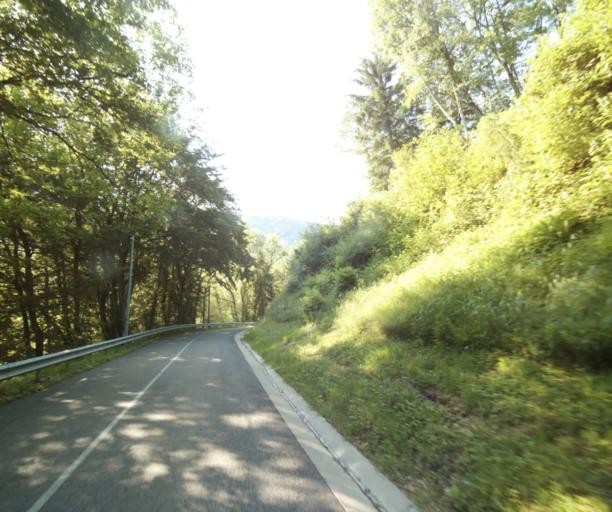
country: FR
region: Rhone-Alpes
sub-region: Departement de la Haute-Savoie
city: Lyaud
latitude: 46.3163
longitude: 6.5054
